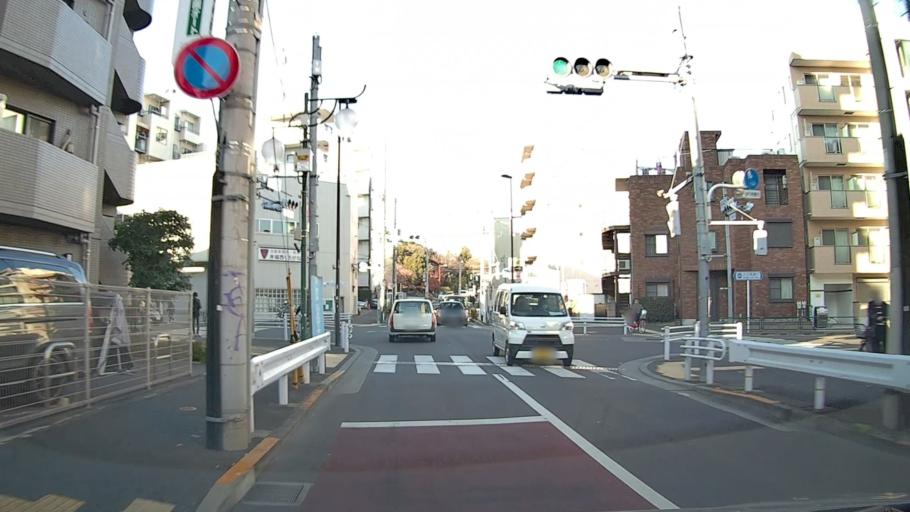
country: JP
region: Tokyo
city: Tokyo
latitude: 35.7022
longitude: 139.6721
